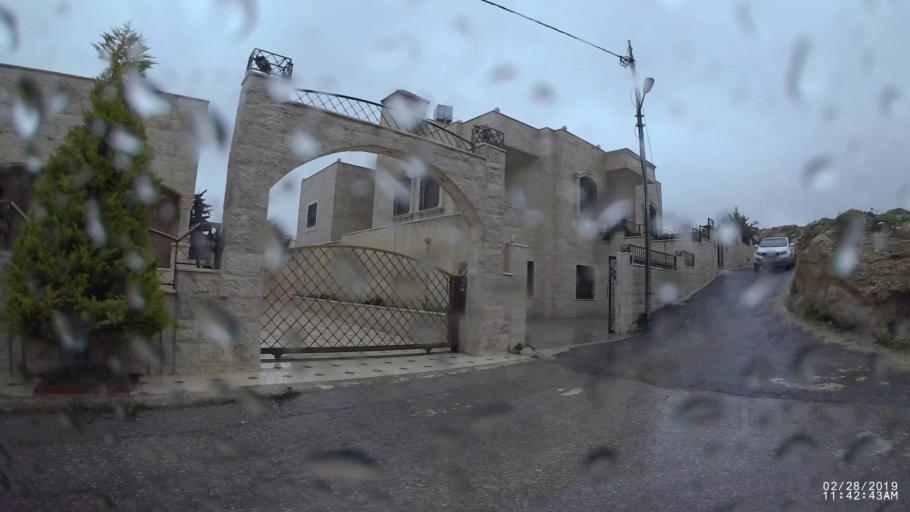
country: JO
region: Amman
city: Al Jubayhah
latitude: 32.0173
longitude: 35.8900
